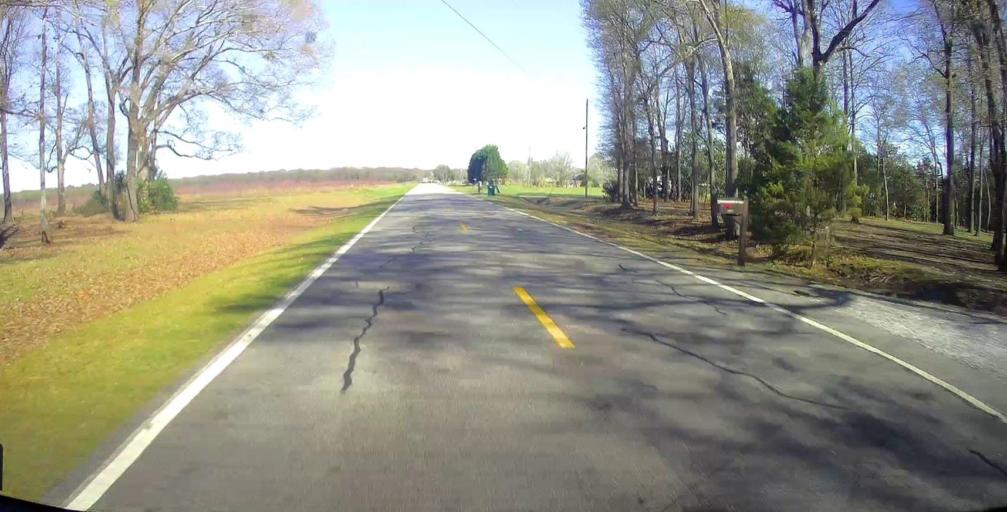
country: US
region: Georgia
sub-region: Peach County
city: Byron
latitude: 32.6446
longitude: -83.8055
